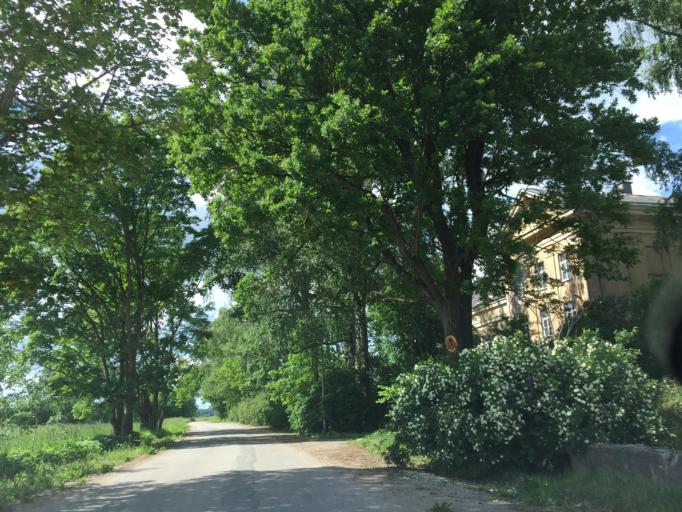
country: LV
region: Dobeles Rajons
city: Dobele
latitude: 56.6860
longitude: 23.4385
